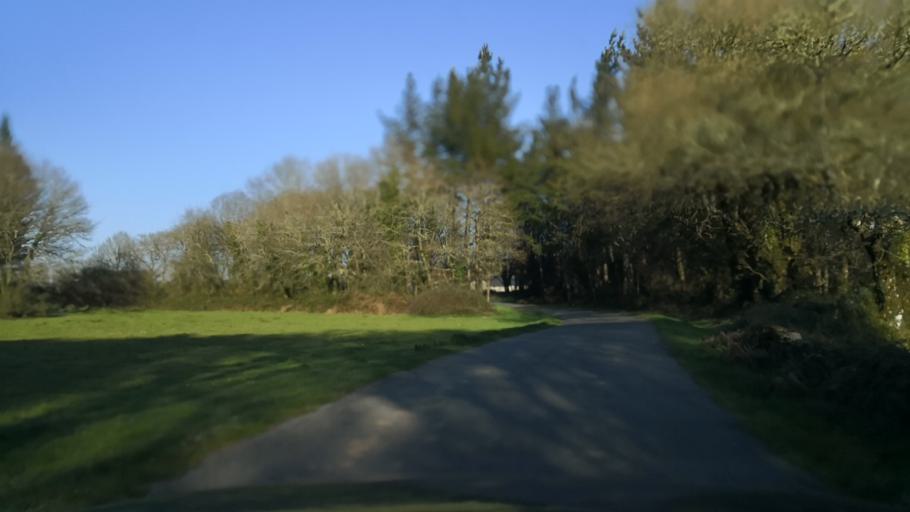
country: ES
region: Galicia
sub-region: Provincia de Lugo
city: Corgo
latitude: 42.9400
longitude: -7.4411
